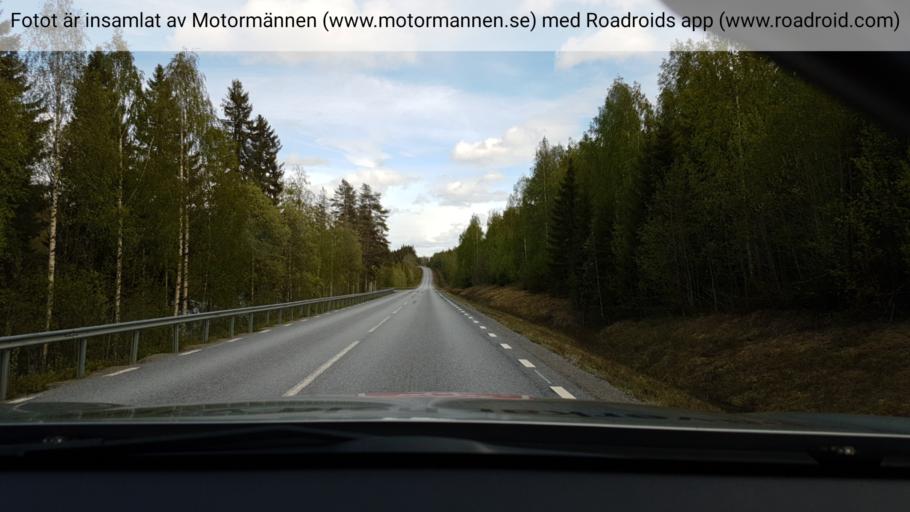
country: SE
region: Vaesterbotten
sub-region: Lycksele Kommun
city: Lycksele
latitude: 64.0385
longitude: 18.5959
